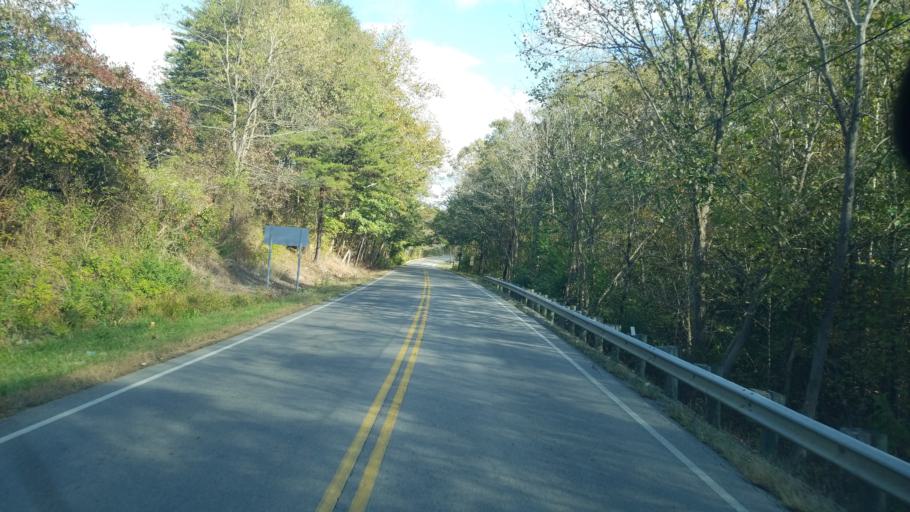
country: US
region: Ohio
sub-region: Jackson County
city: Wellston
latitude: 39.1165
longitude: -82.5573
